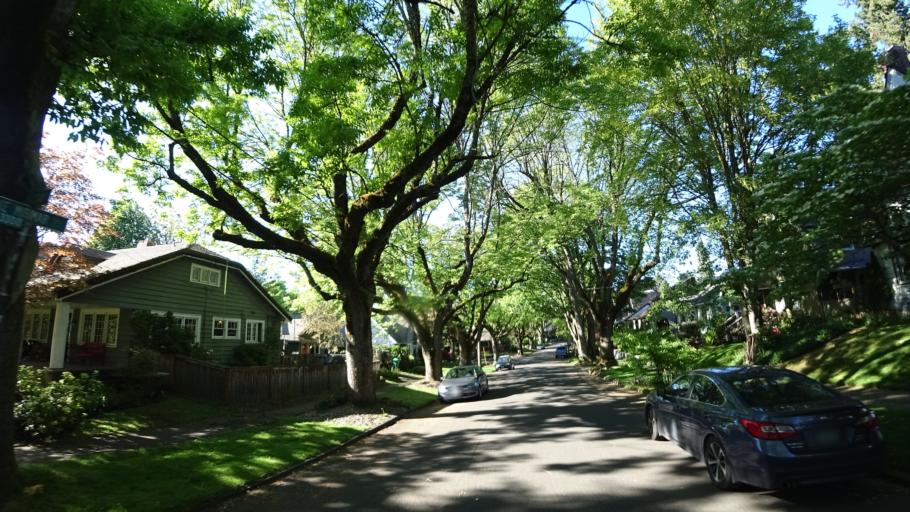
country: US
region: Oregon
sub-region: Multnomah County
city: Portland
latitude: 45.5266
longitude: -122.6302
